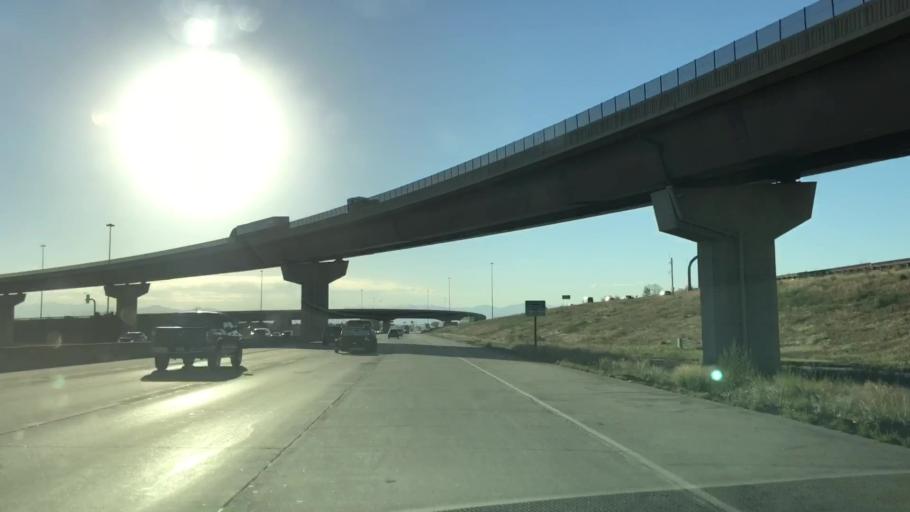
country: US
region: Colorado
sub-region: Adams County
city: Aurora
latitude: 39.7729
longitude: -104.8252
